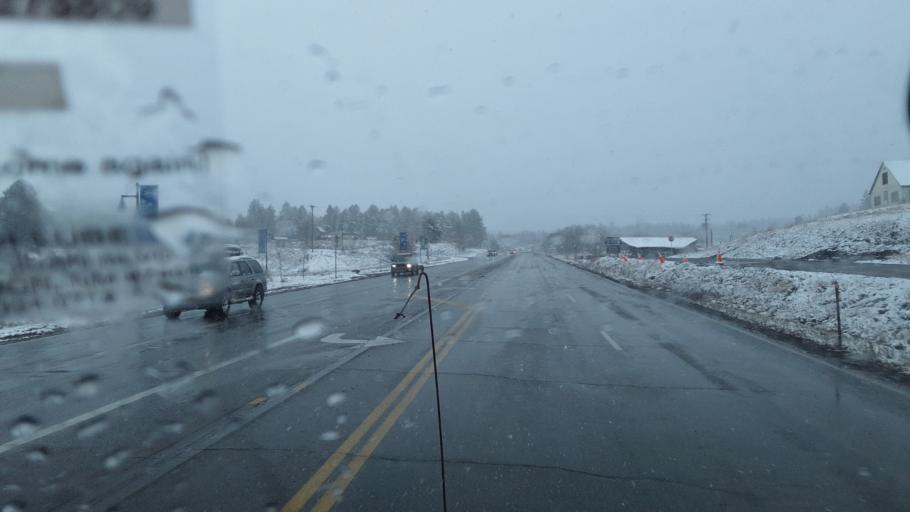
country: US
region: Colorado
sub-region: Archuleta County
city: Pagosa Springs
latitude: 37.2667
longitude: -107.0177
